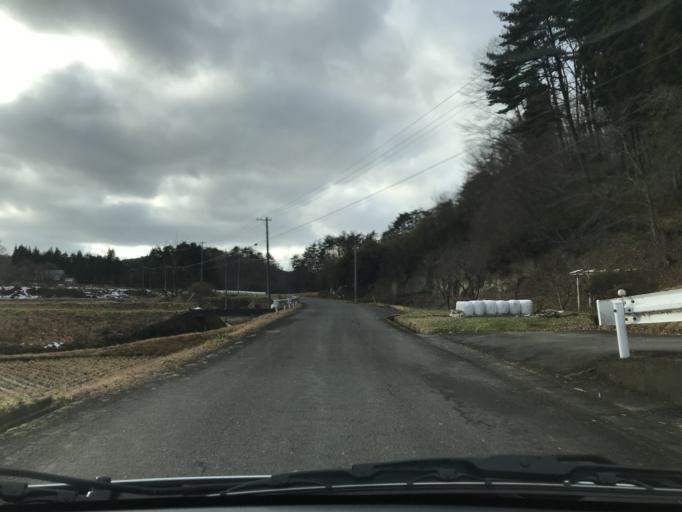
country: JP
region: Iwate
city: Ichinoseki
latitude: 38.9979
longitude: 141.0017
